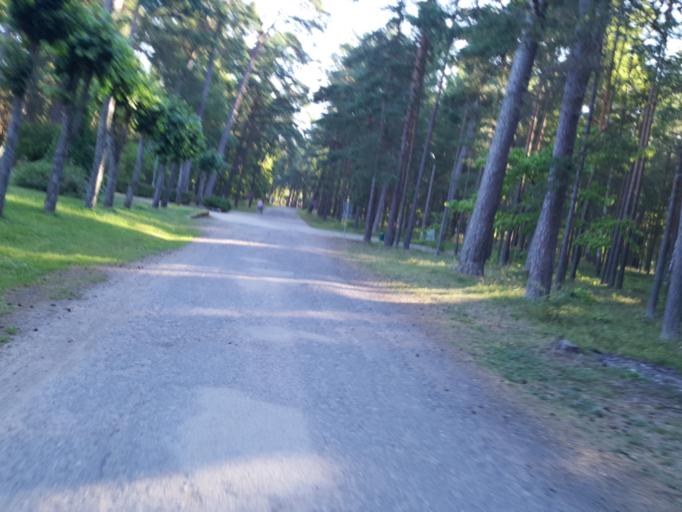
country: LV
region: Salacgrivas
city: Ainazi
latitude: 57.8609
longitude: 24.3524
